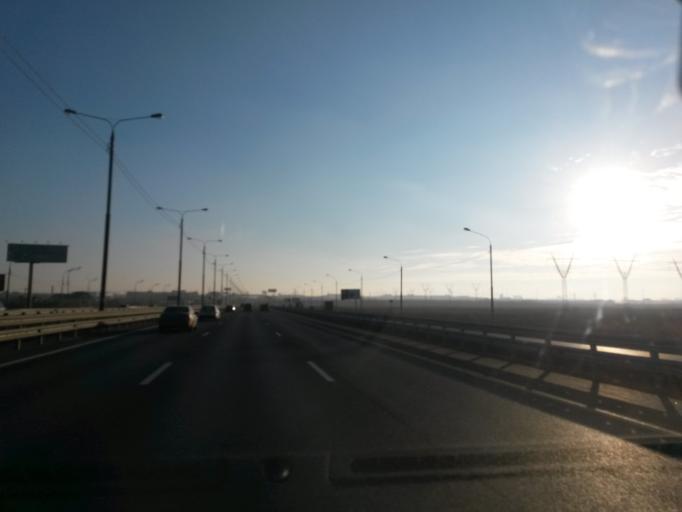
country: RU
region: Moskovskaya
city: Shcherbinka
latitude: 55.4583
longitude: 37.6191
